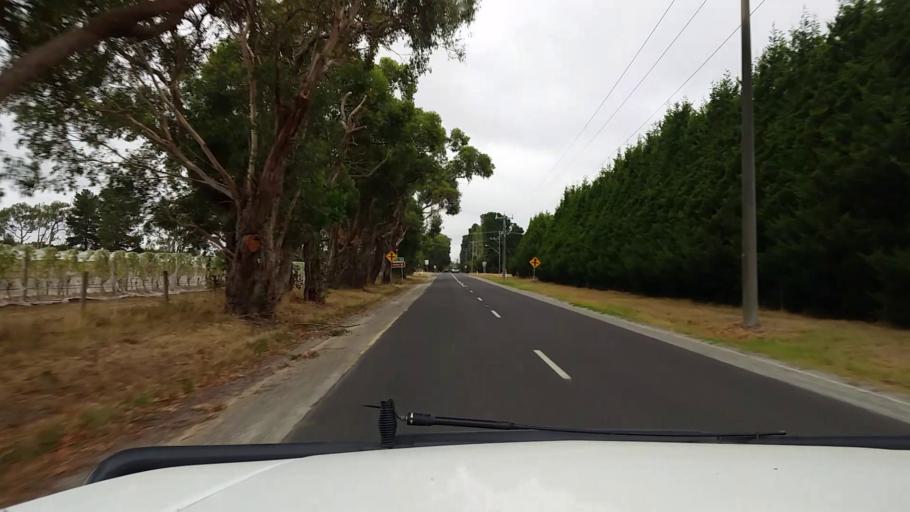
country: AU
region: Victoria
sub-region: Mornington Peninsula
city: Balnarring
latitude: -38.3405
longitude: 145.1457
